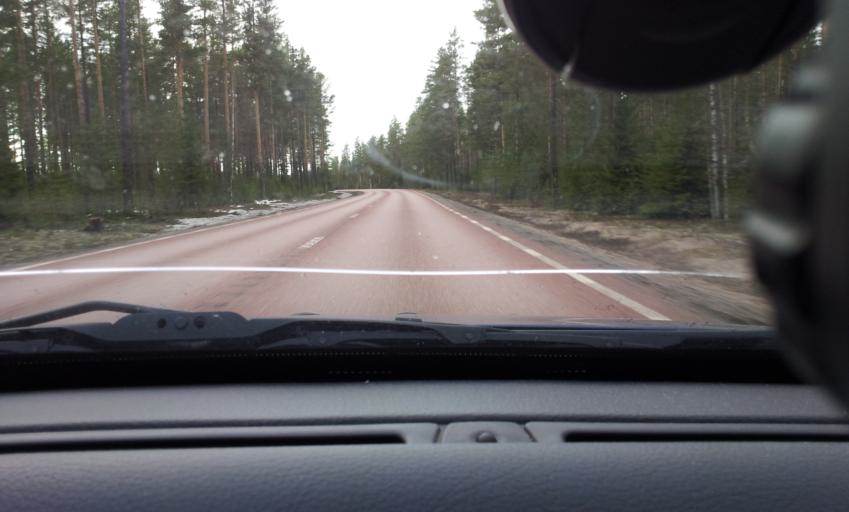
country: SE
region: Gaevleborg
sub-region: Ljusdals Kommun
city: Farila
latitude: 61.9178
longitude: 15.6171
